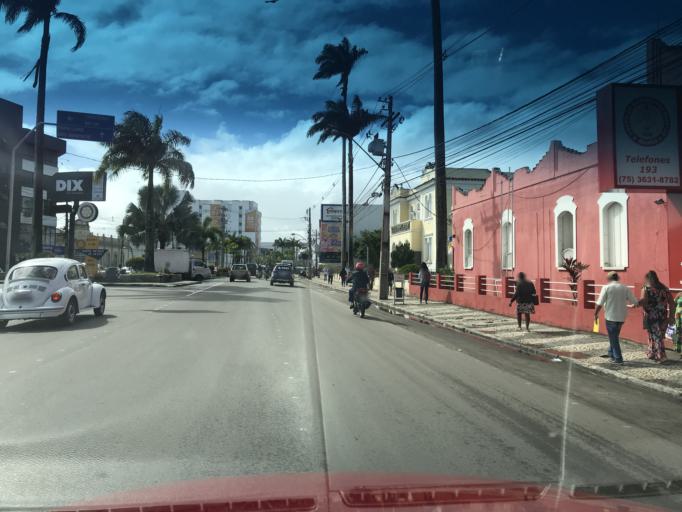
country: BR
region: Bahia
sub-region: Santo Antonio De Jesus
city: Santo Antonio de Jesus
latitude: -12.9662
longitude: -39.2663
